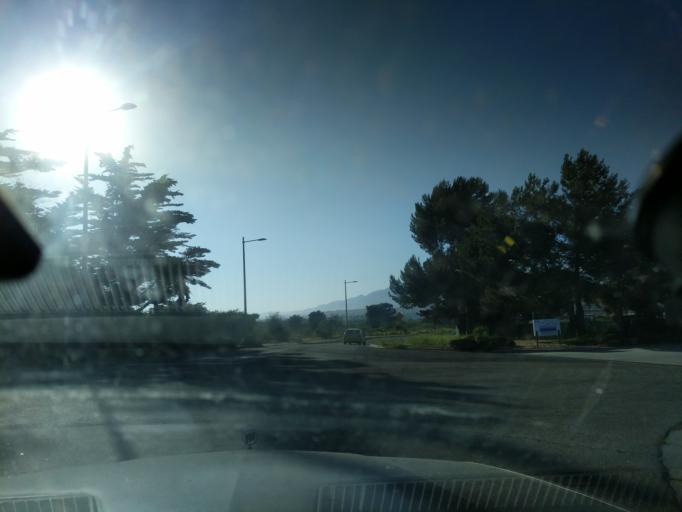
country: US
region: California
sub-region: Santa Barbara County
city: Isla Vista
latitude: 34.4217
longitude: -119.8532
